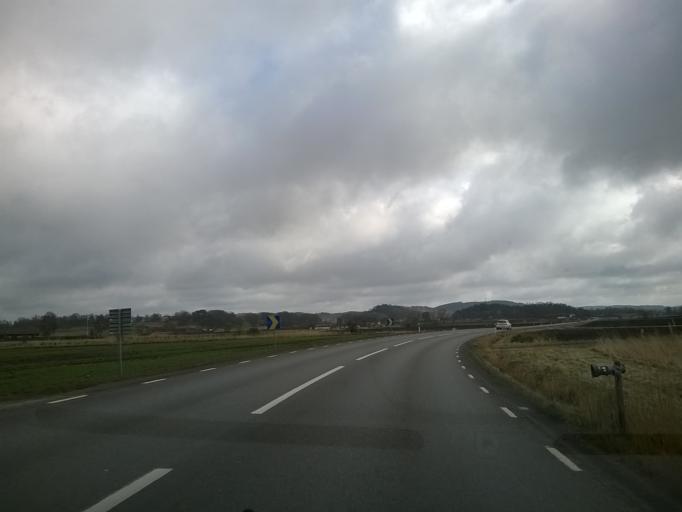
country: SE
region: Halland
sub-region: Varbergs Kommun
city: Tvaaker
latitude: 57.1389
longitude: 12.4002
